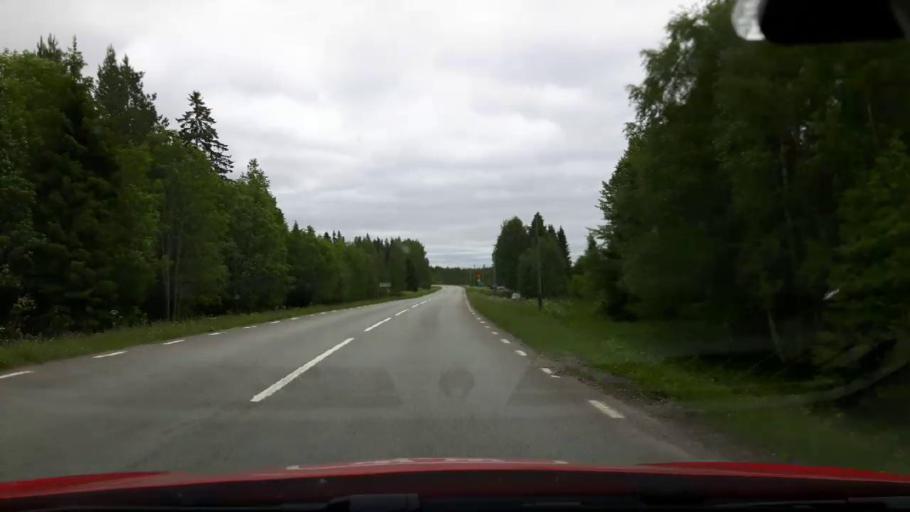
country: SE
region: Jaemtland
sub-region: Stroemsunds Kommun
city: Stroemsund
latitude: 63.5350
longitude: 15.4470
